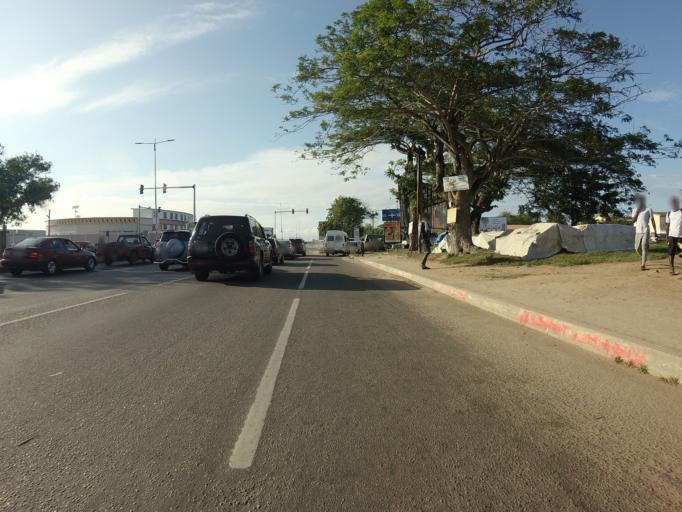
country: GH
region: Greater Accra
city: Accra
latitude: 5.5377
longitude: -0.2219
